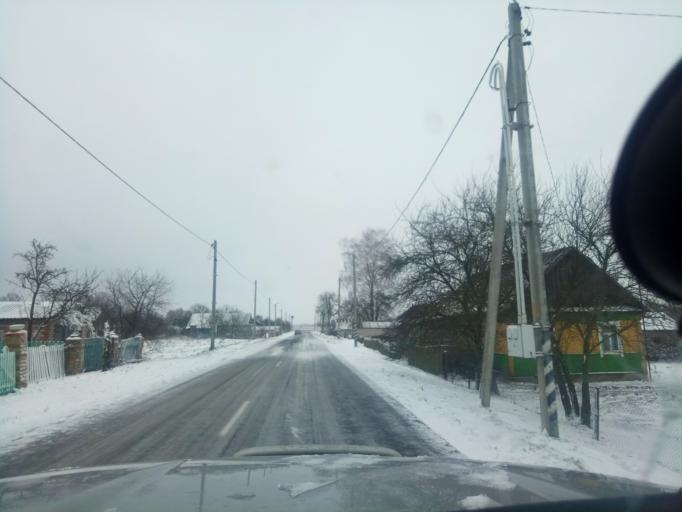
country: BY
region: Minsk
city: Klyetsk
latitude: 53.0542
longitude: 26.7786
